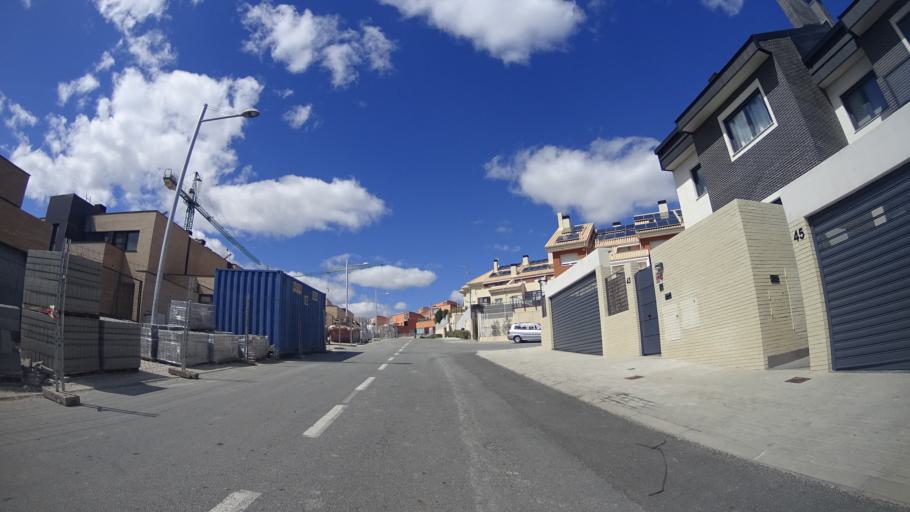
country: ES
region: Madrid
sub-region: Provincia de Madrid
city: Torrelodones
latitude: 40.5635
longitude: -3.9191
